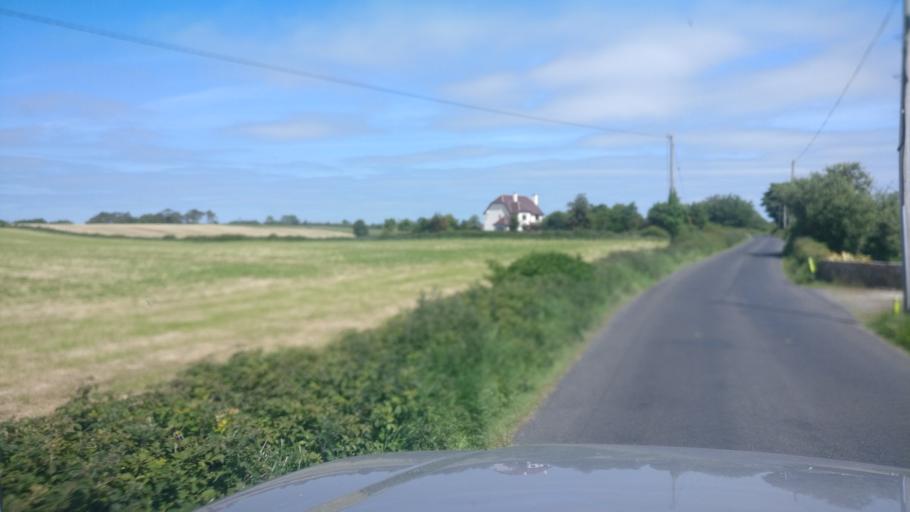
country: IE
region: Connaught
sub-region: County Galway
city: Gort
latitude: 53.1483
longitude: -8.7576
